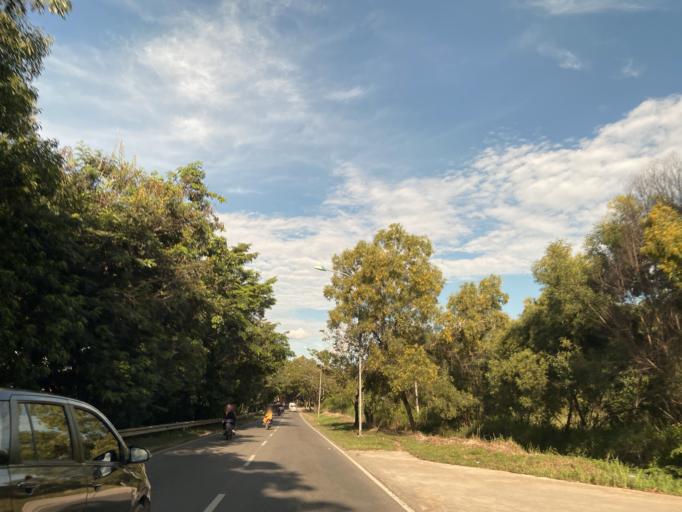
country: SG
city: Singapore
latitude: 1.1230
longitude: 104.0112
